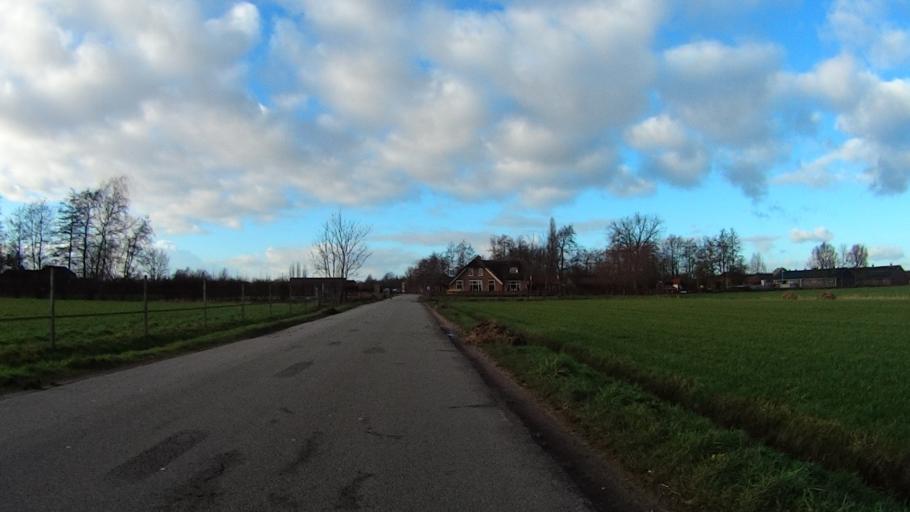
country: NL
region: Gelderland
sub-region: Gemeente Barneveld
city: Zwartebroek
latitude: 52.1855
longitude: 5.4963
